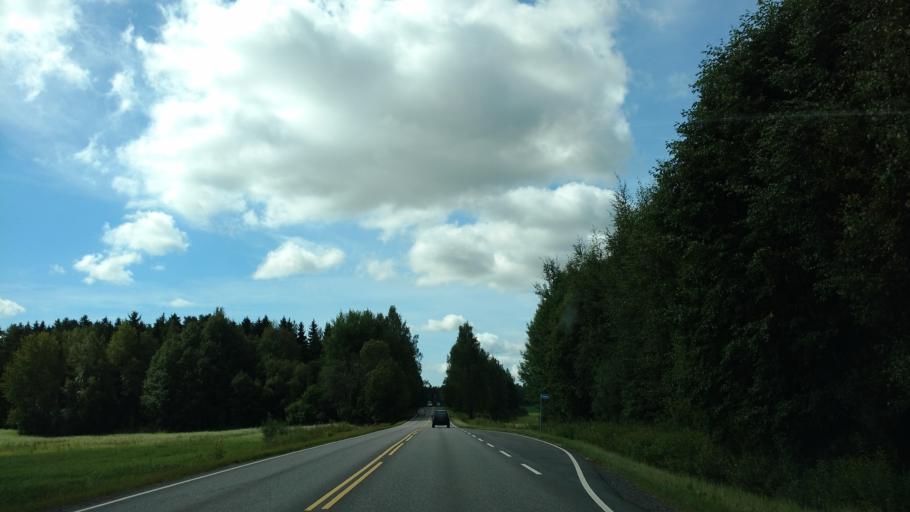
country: FI
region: Varsinais-Suomi
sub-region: Salo
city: Pernioe
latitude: 60.1917
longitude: 23.0666
